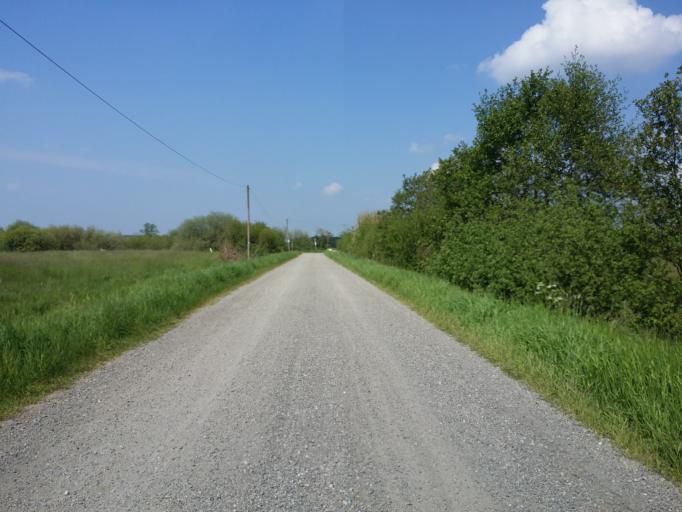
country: DE
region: Lower Saxony
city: Osterholz-Scharmbeck
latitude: 53.2208
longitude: 8.8466
